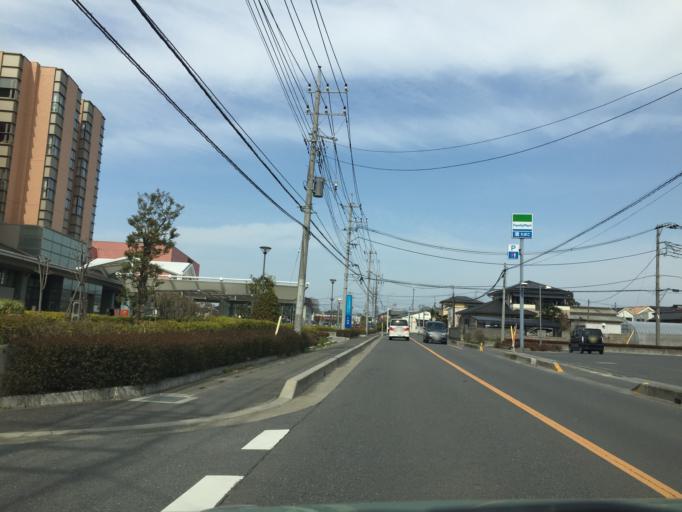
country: JP
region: Saitama
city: Yono
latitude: 35.8811
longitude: 139.5989
